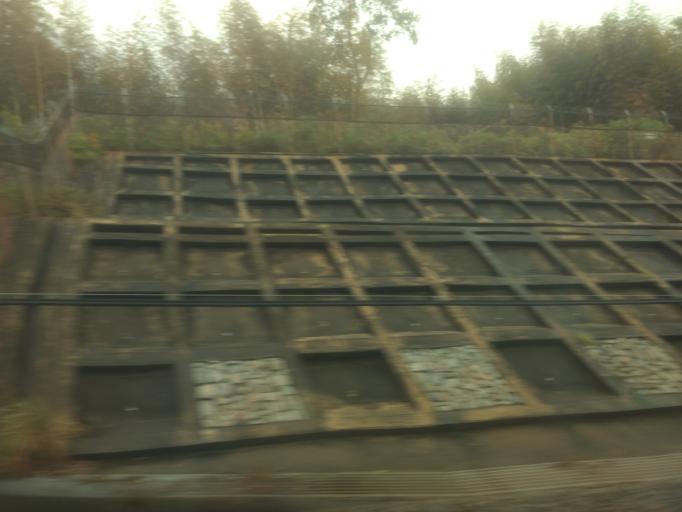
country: JP
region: Yamaguchi
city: Kudamatsu
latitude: 34.0349
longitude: 131.8531
